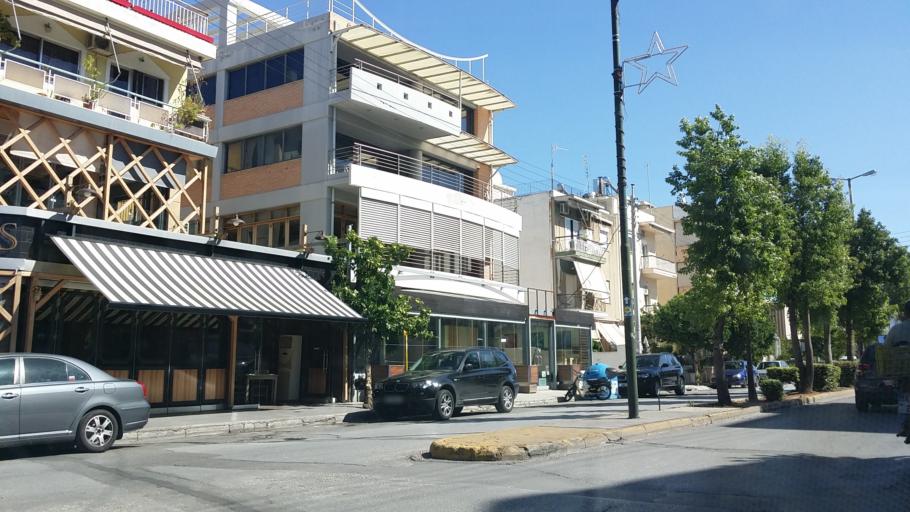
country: GR
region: Attica
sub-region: Nomarchia Athinas
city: Peristeri
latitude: 38.0124
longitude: 23.7070
